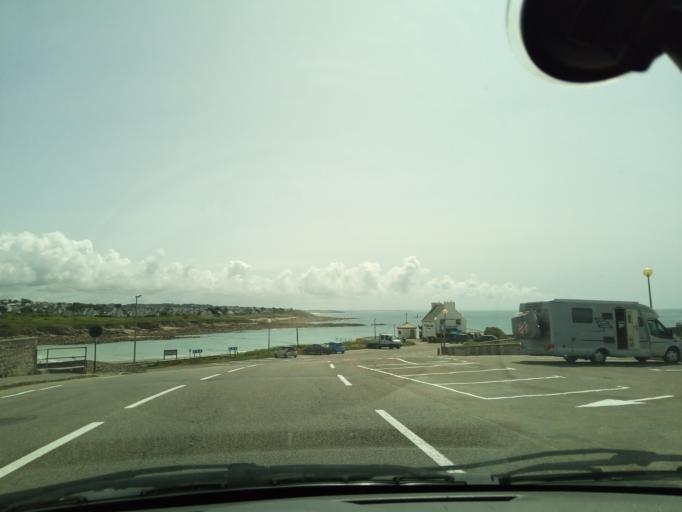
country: FR
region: Brittany
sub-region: Departement du Finistere
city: Audierne
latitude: 48.0118
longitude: -4.5427
